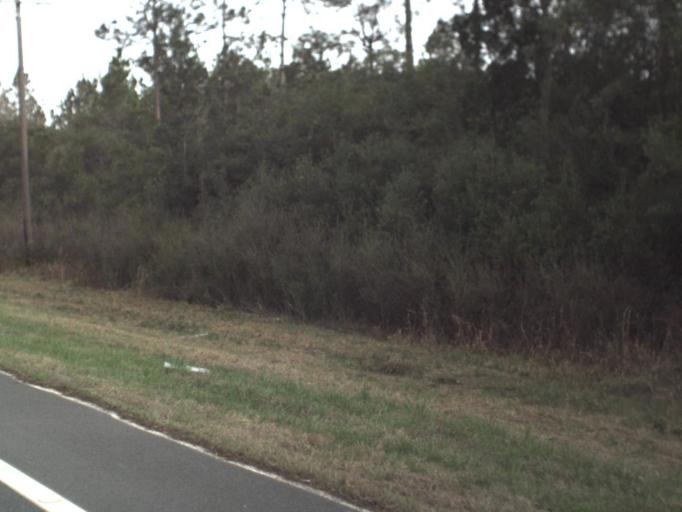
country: US
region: Florida
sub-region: Gulf County
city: Wewahitchka
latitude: 30.1395
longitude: -85.2562
